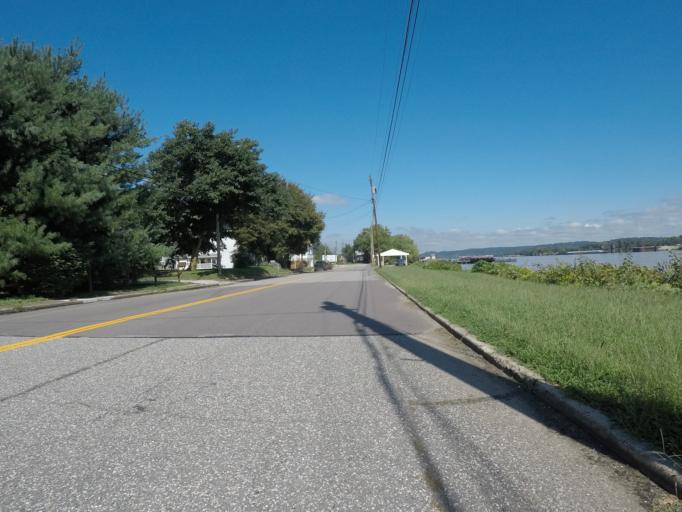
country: US
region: Ohio
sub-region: Lawrence County
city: South Point
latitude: 38.4258
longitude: -82.6011
